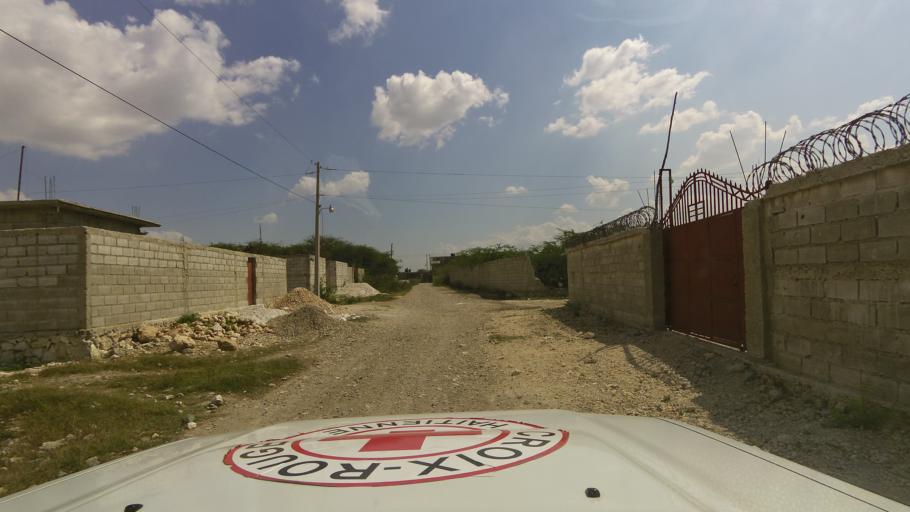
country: HT
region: Ouest
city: Croix des Bouquets
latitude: 18.6410
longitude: -72.2641
